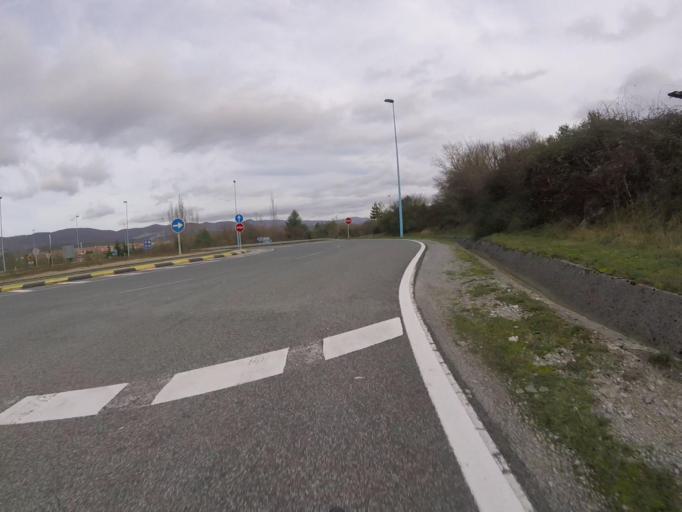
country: ES
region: Navarre
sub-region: Provincia de Navarra
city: Olazagutia
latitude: 42.8840
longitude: -2.1772
